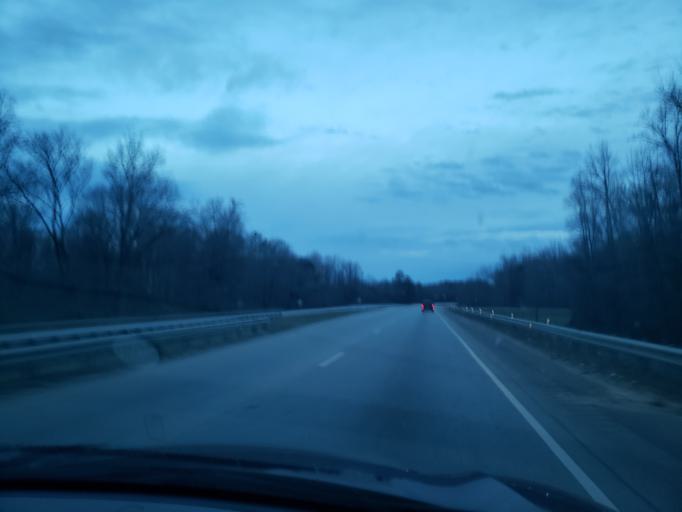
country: US
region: Alabama
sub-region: Lee County
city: Auburn
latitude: 32.6578
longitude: -85.4600
